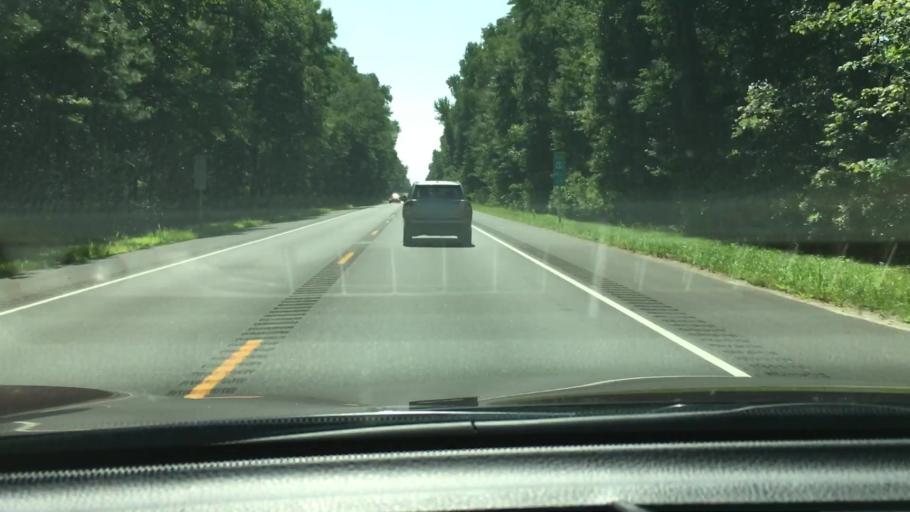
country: US
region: New Jersey
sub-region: Cape May County
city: Woodbine
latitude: 39.3336
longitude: -74.8808
